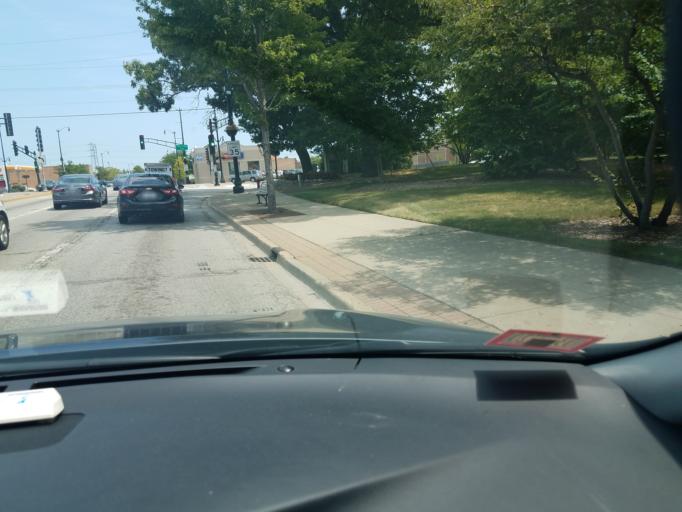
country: US
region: Illinois
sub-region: Cook County
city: Morton Grove
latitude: 42.0408
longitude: -87.7574
